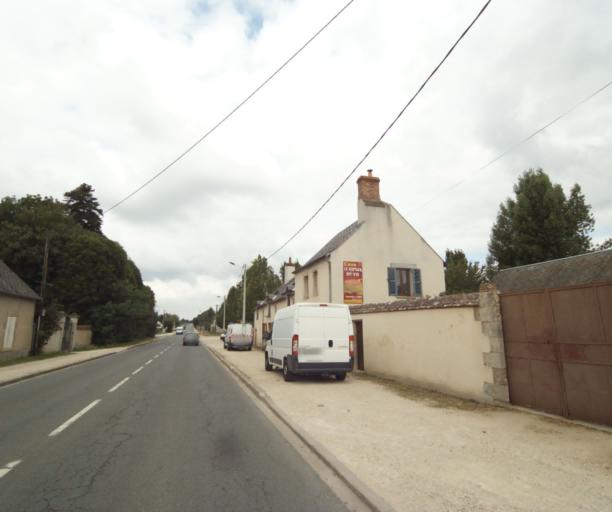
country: FR
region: Centre
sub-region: Departement du Loiret
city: Checy
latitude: 47.8987
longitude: 2.0177
